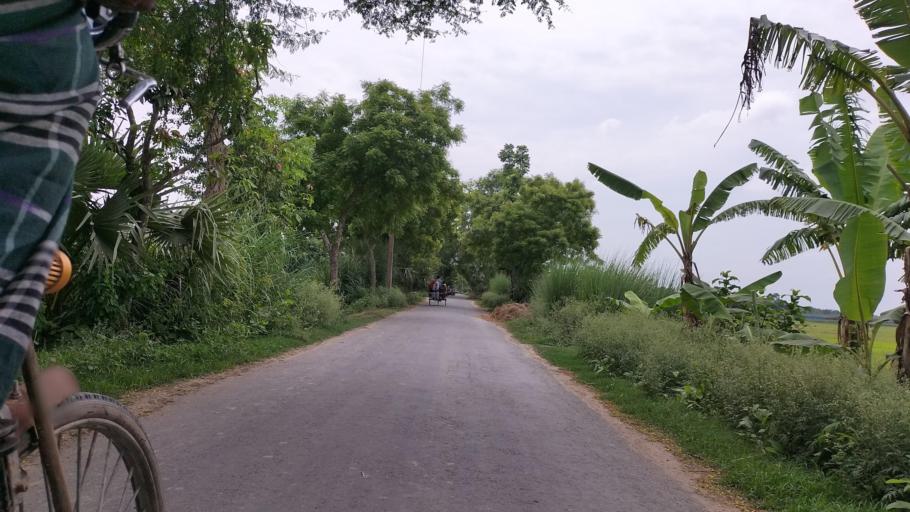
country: BD
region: Rajshahi
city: Rajshahi
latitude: 24.5135
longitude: 88.6346
